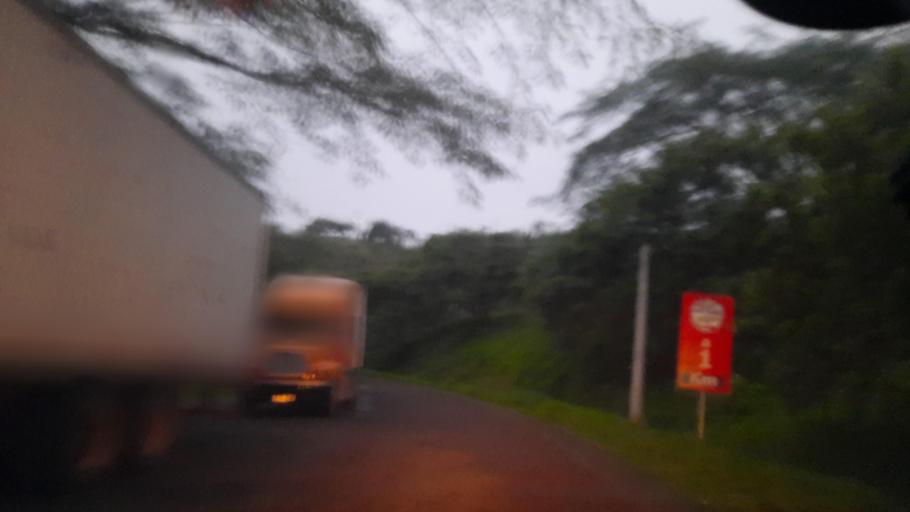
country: GT
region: Jutiapa
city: Atescatempa
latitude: 14.2169
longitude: -89.6892
